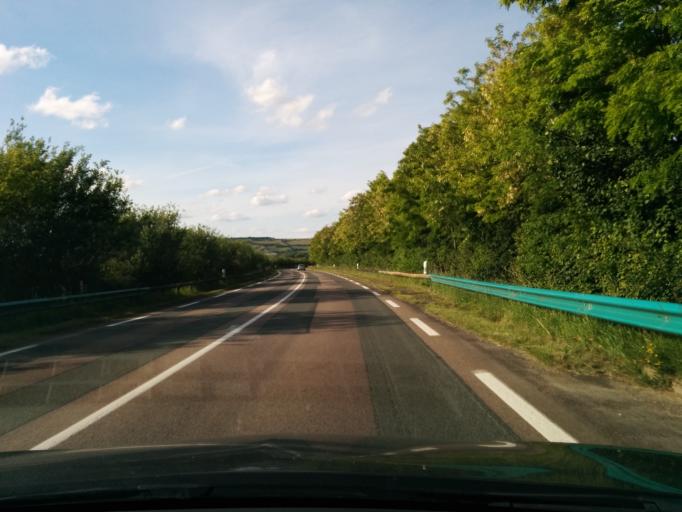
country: FR
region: Haute-Normandie
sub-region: Departement de l'Eure
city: Les Andelys
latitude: 49.2196
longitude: 1.3950
